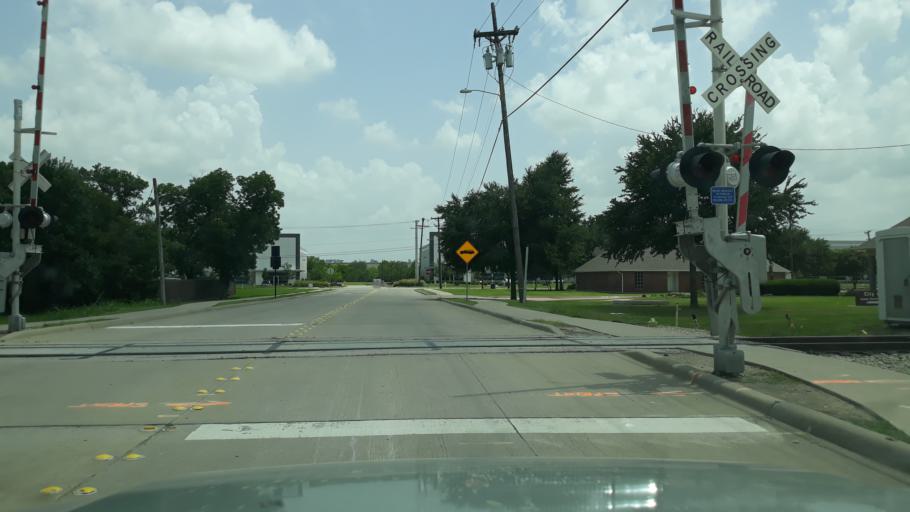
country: US
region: Texas
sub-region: Dallas County
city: Coppell
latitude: 32.9499
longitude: -97.0052
